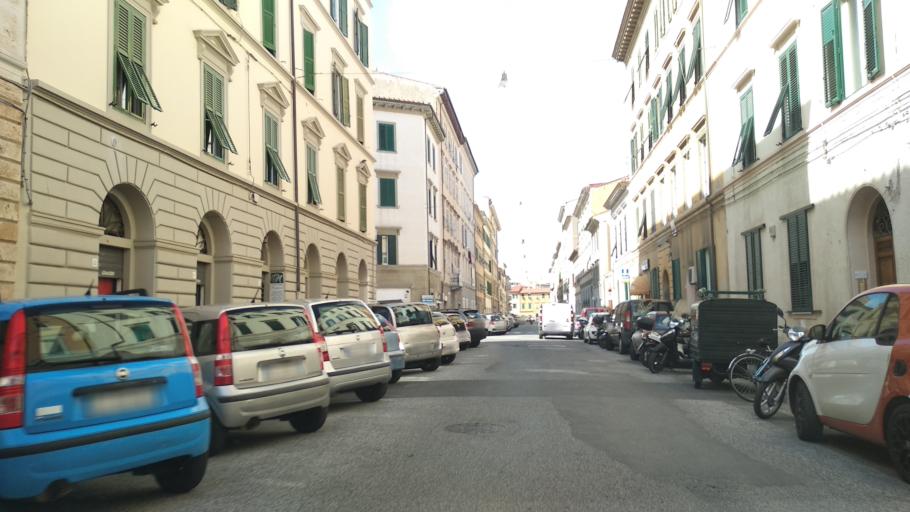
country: IT
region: Tuscany
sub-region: Provincia di Livorno
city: Livorno
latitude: 43.5479
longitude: 10.3187
